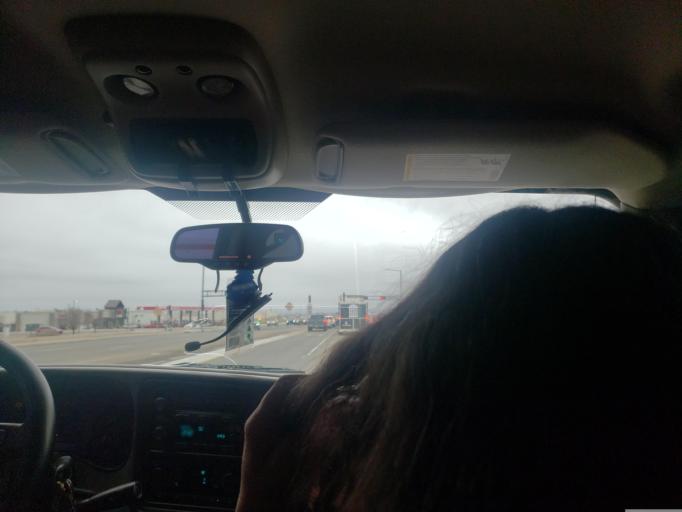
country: US
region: New Mexico
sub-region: Bernalillo County
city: Albuquerque
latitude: 35.0875
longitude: -106.7281
